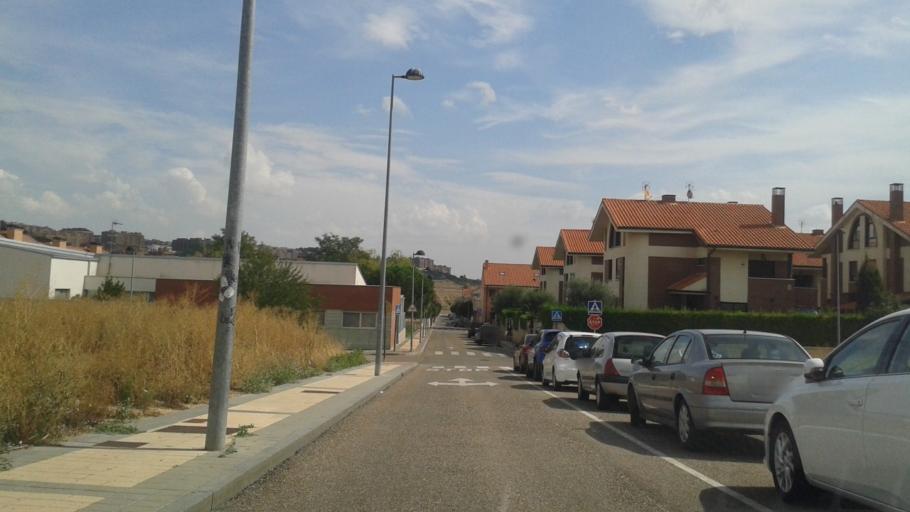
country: ES
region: Castille and Leon
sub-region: Provincia de Valladolid
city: Arroyo
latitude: 41.6295
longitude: -4.7767
